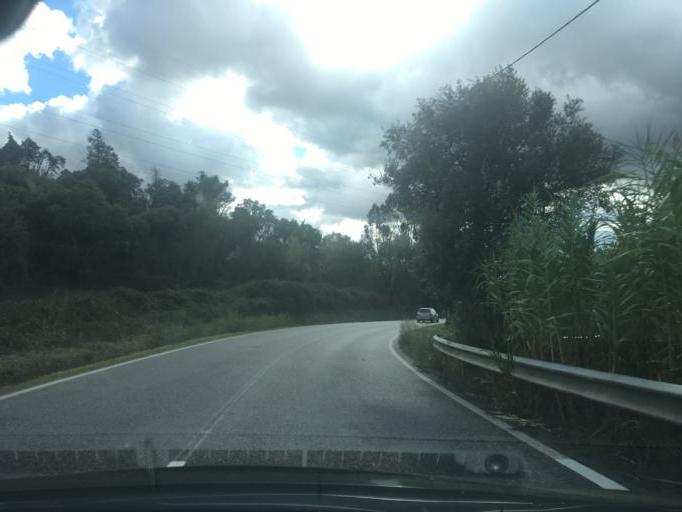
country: PT
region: Santarem
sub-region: Torres Novas
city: Riachos
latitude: 39.4574
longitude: -8.5204
